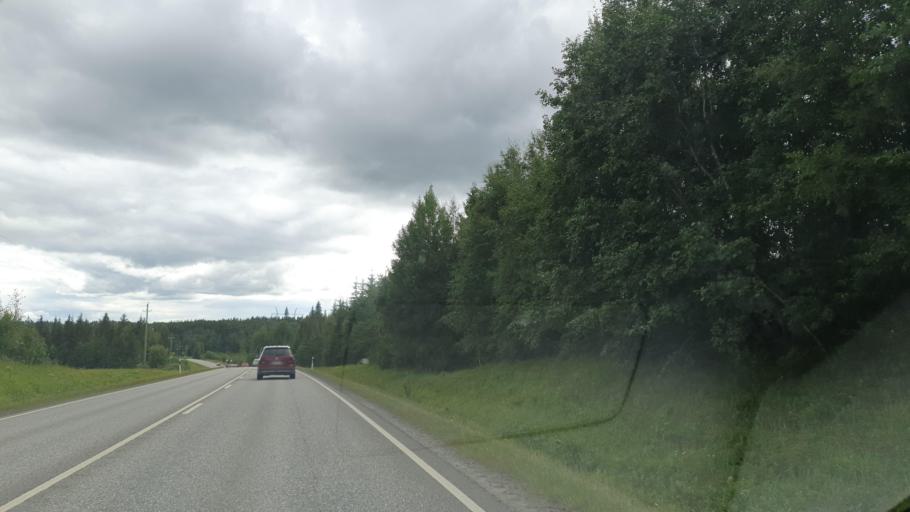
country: FI
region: Northern Savo
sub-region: Ylae-Savo
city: Sonkajaervi
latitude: 63.7124
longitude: 27.3606
